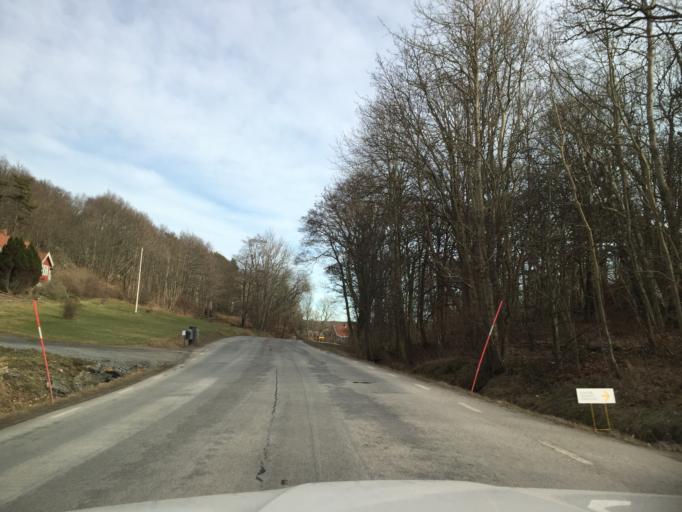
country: SE
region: Vaestra Goetaland
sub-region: Tjorns Kommun
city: Skaerhamn
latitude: 58.0348
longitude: 11.5708
